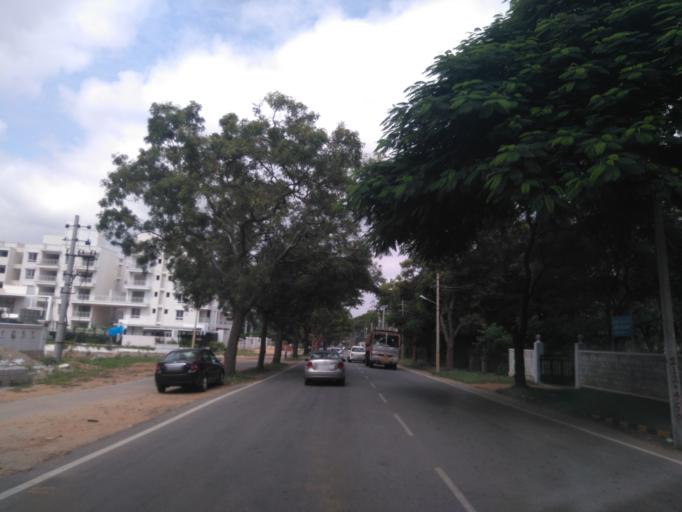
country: IN
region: Karnataka
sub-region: Mysore
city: Mysore
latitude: 12.3005
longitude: 76.6838
